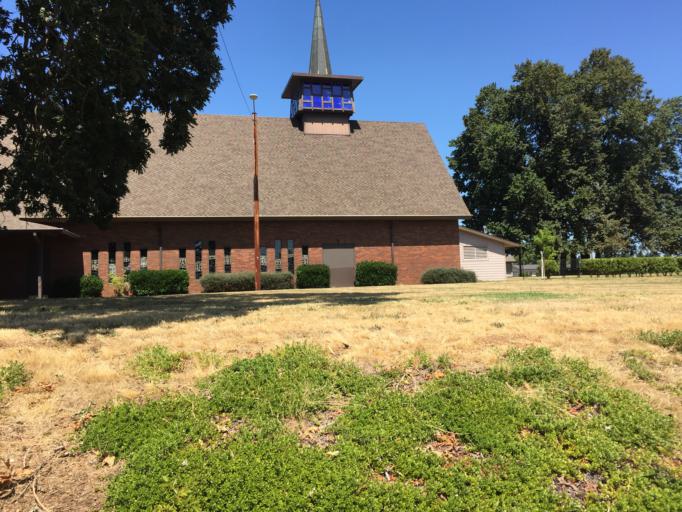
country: US
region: Oregon
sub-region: Clackamas County
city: Oregon City
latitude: 45.3365
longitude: -122.6035
